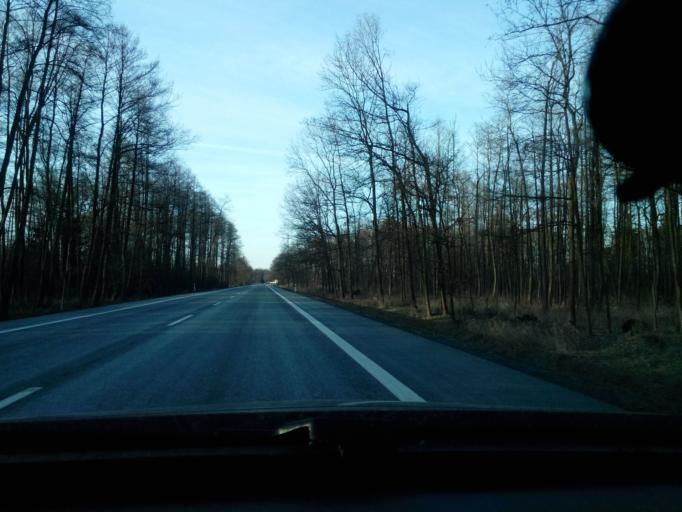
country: PL
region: Lodz Voivodeship
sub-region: Powiat kutnowski
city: Ostrowy
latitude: 52.3487
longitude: 19.1457
